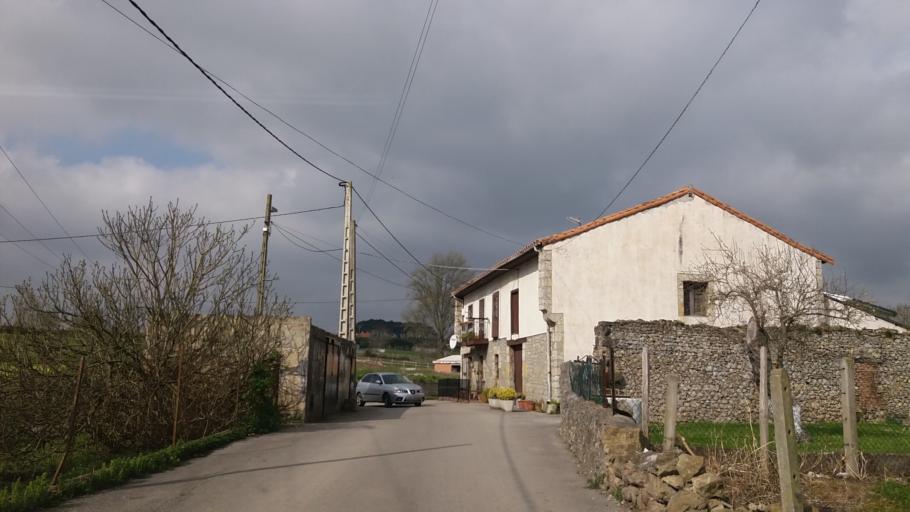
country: ES
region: Cantabria
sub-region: Provincia de Cantabria
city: Reocin
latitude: 43.3680
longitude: -4.0877
